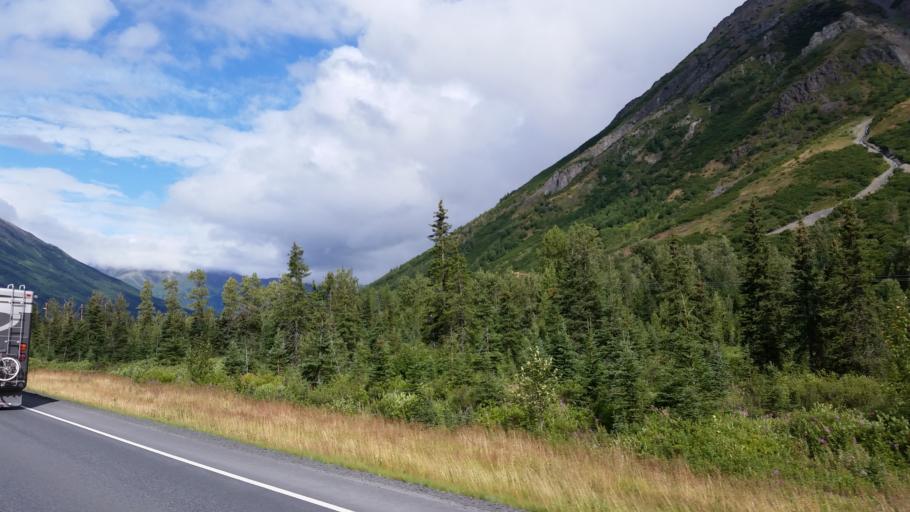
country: US
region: Alaska
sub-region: Anchorage Municipality
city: Girdwood
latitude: 60.7279
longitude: -149.3075
